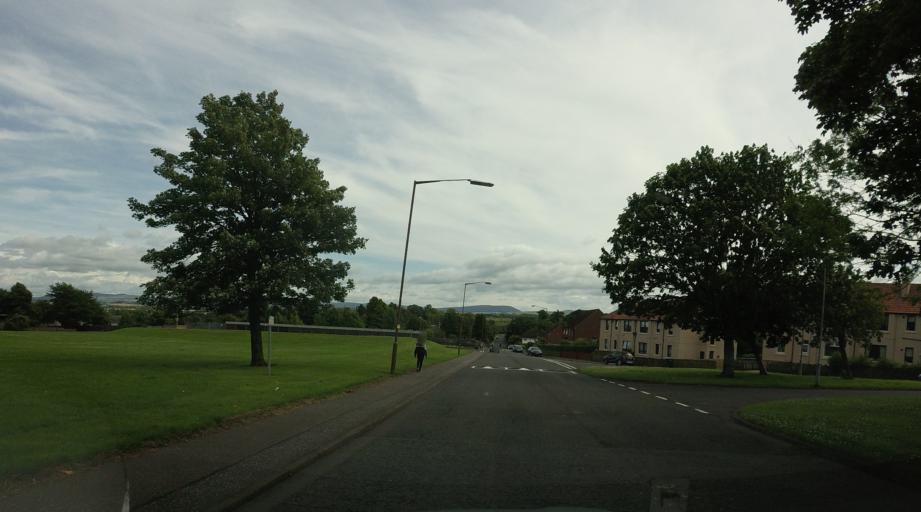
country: GB
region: Scotland
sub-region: West Lothian
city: Broxburn
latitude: 55.9335
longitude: -3.4999
